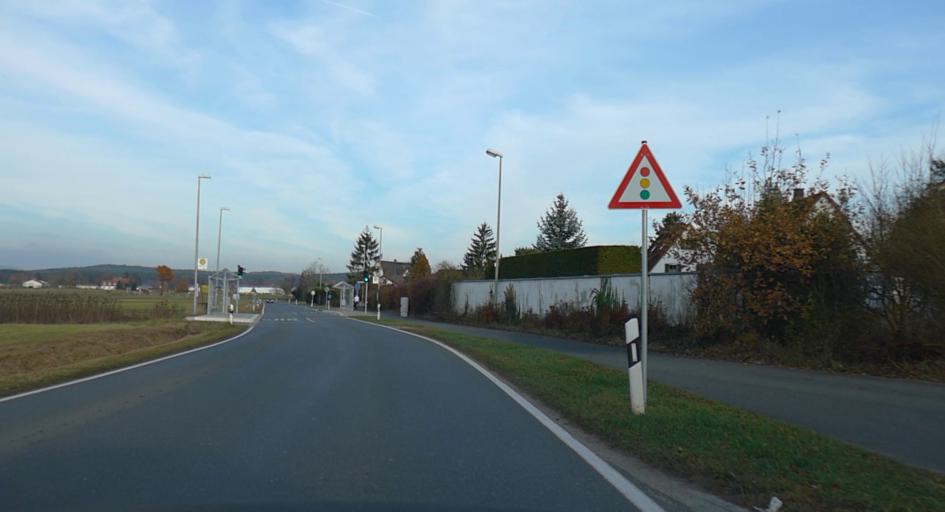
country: DE
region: Bavaria
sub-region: Upper Franconia
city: Poxdorf
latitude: 49.6584
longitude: 11.0569
